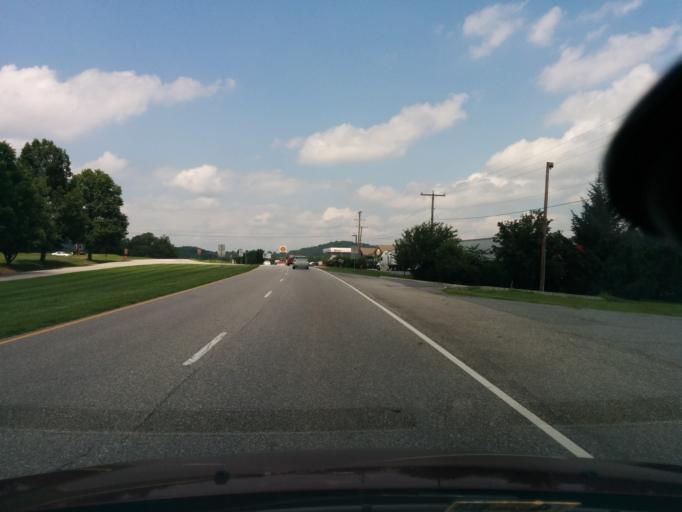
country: US
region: Virginia
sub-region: Rockbridge County
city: East Lexington
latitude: 37.8309
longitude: -79.3795
